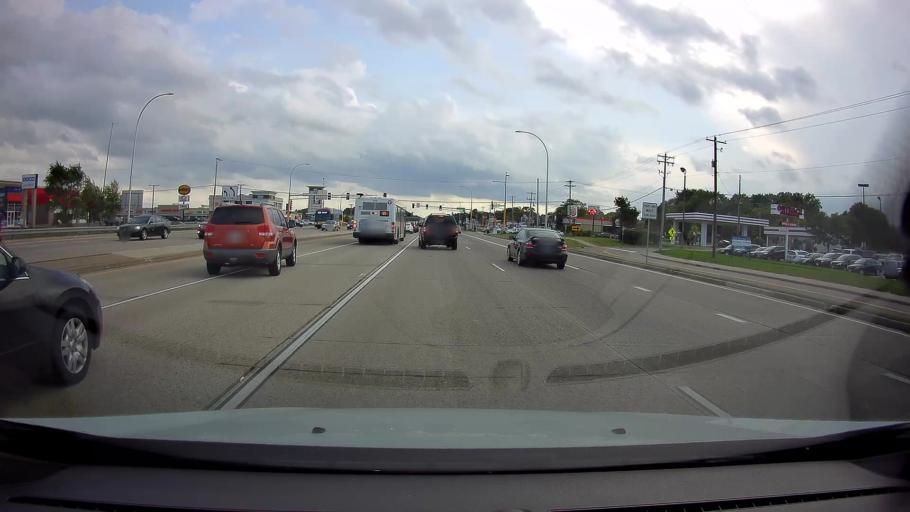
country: US
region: Minnesota
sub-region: Ramsey County
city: Roseville
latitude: 45.0073
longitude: -93.1666
